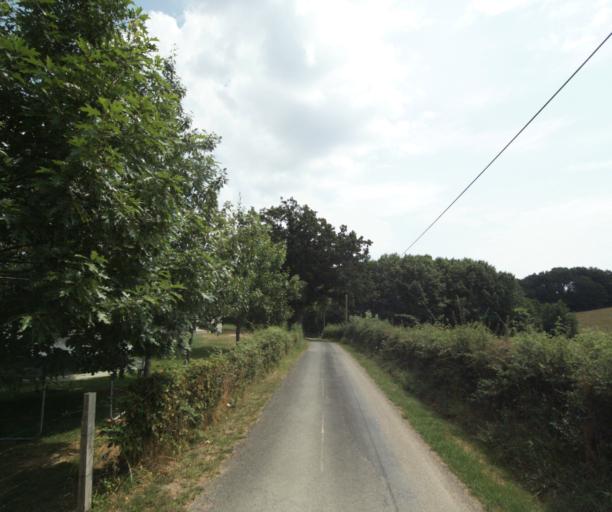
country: FR
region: Bourgogne
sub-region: Departement de Saone-et-Loire
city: Gueugnon
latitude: 46.5902
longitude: 4.0161
